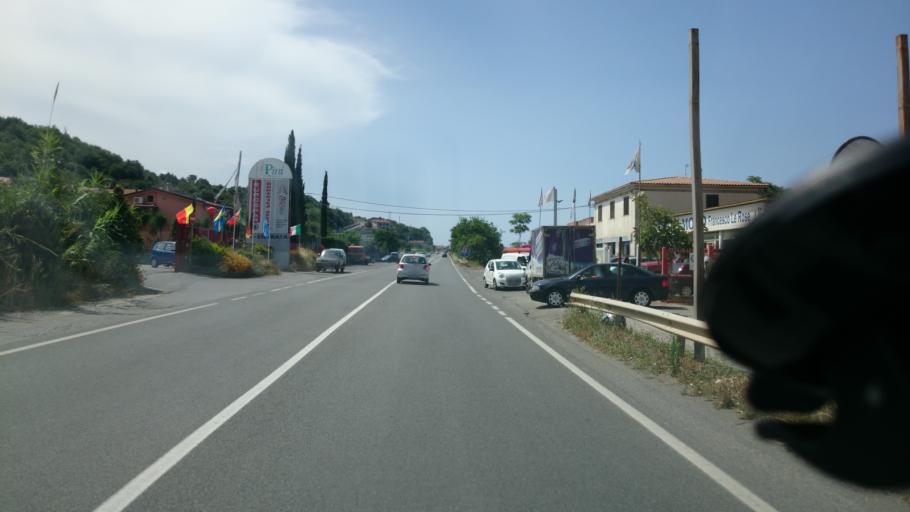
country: IT
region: Calabria
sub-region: Provincia di Cosenza
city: Diamante
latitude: 39.6870
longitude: 15.8188
